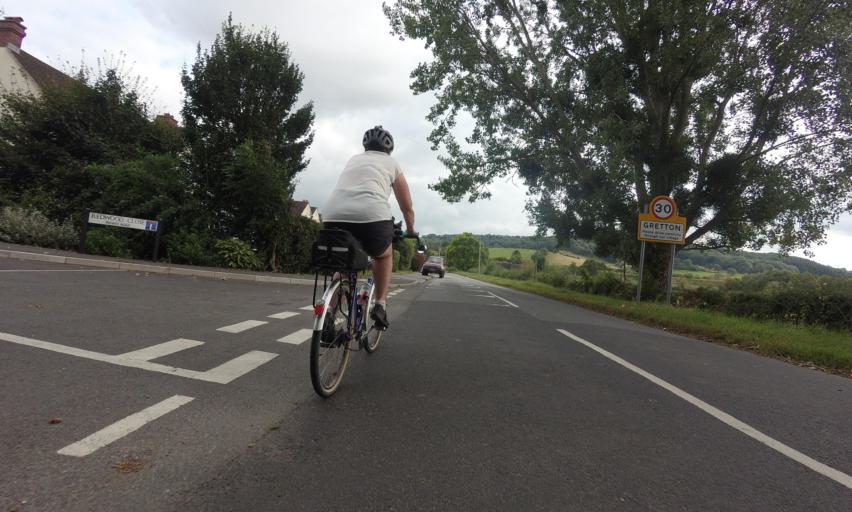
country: GB
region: England
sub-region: Gloucestershire
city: Winchcombe
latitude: 51.9745
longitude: -1.9950
